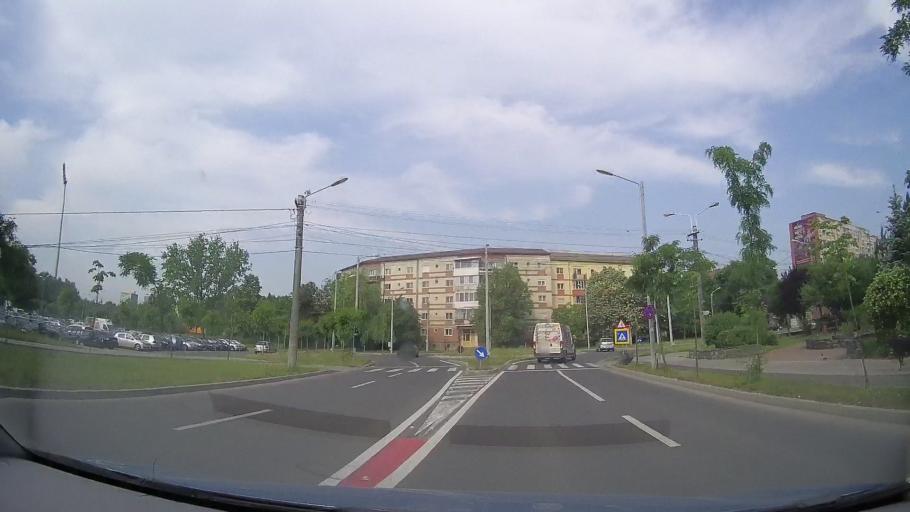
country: RO
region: Timis
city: Timisoara
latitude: 45.7427
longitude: 21.2440
